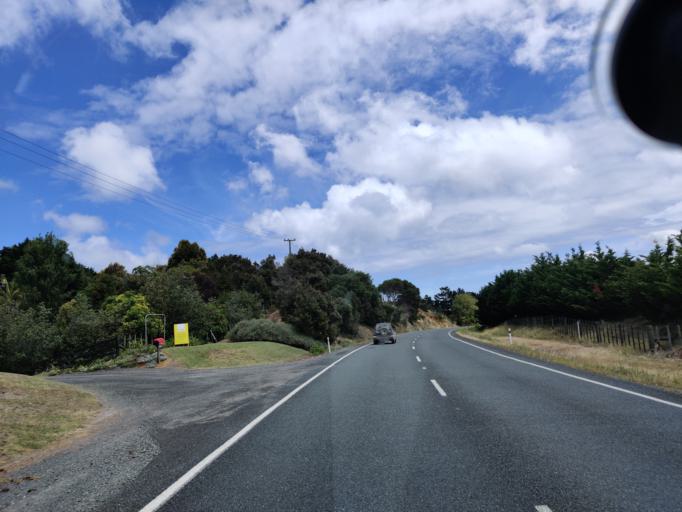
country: NZ
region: Northland
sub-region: Far North District
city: Kaitaia
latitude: -34.8960
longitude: 173.1688
